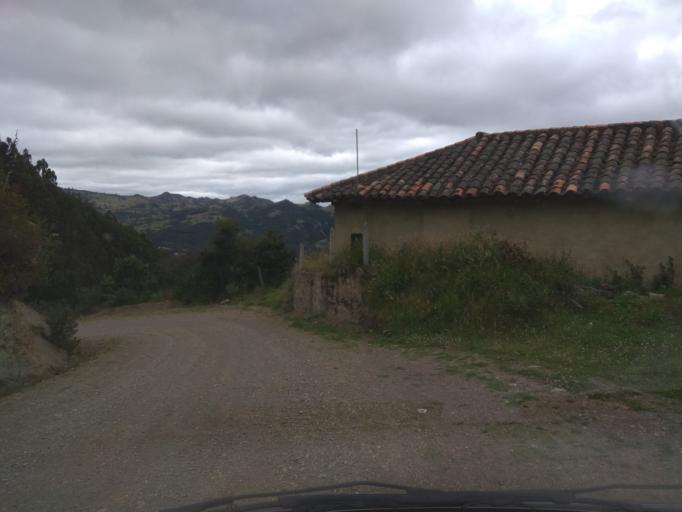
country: CO
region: Boyaca
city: Mongui
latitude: 5.7335
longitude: -72.8340
